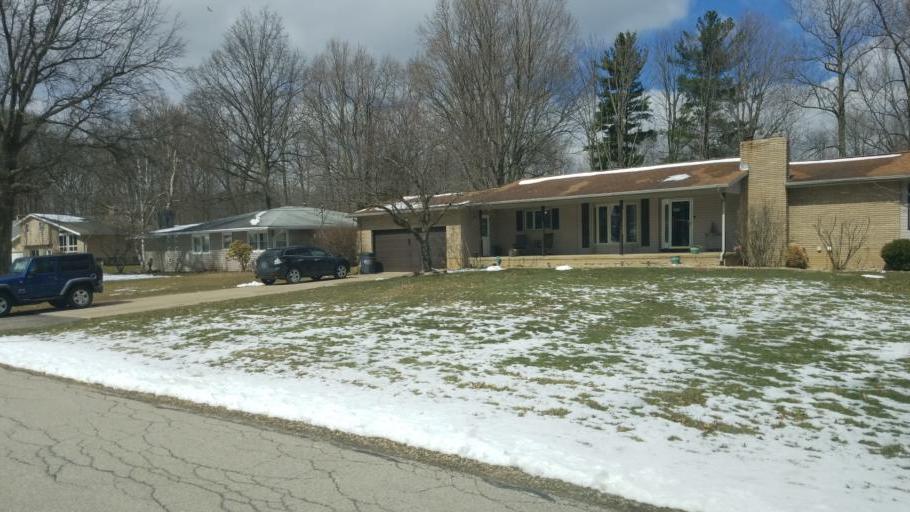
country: US
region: Ohio
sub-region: Richland County
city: Ontario
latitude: 40.7751
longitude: -82.6442
